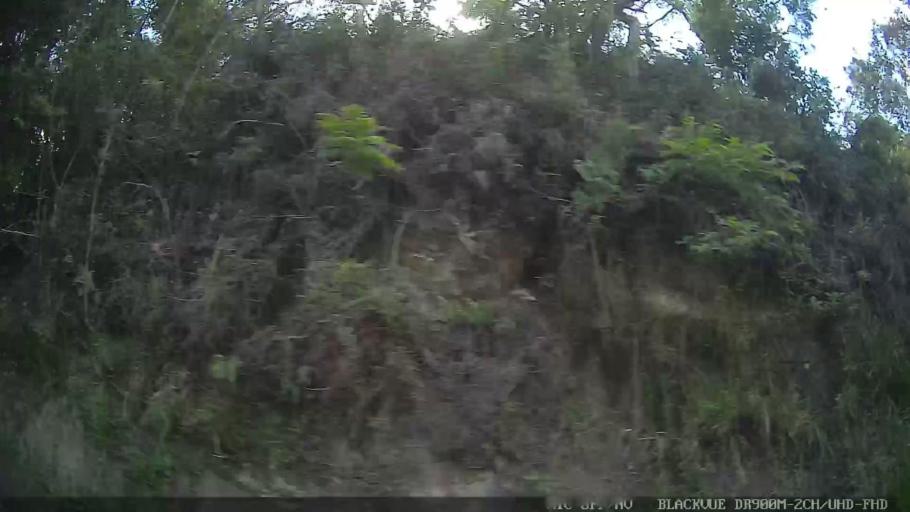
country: BR
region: Sao Paulo
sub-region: Santa Branca
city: Santa Branca
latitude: -23.5277
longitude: -45.7559
